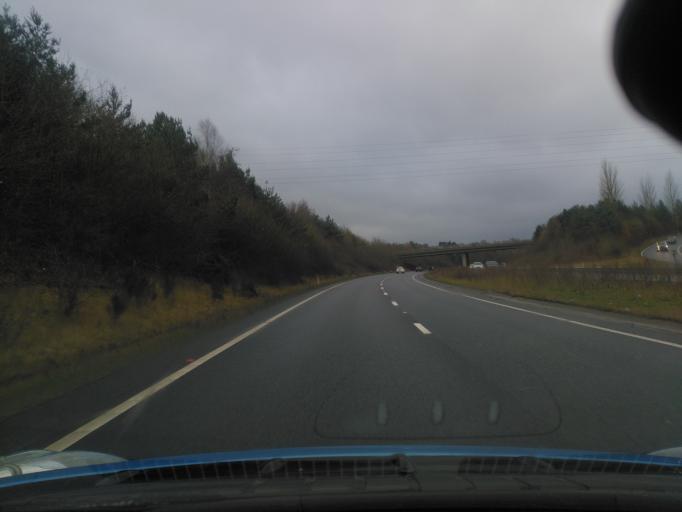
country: GB
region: England
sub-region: Surrey
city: Milford
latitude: 51.1808
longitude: -0.6513
